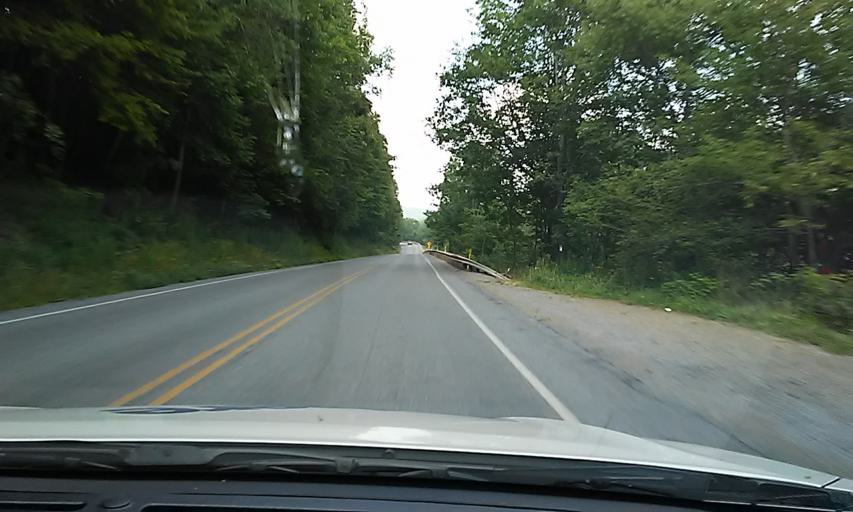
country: US
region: New York
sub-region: Allegany County
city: Wellsville
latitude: 41.9545
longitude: -77.8590
